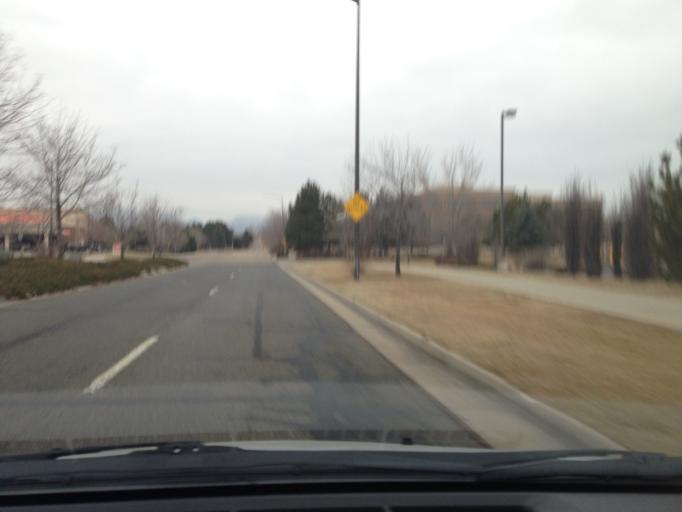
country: US
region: Colorado
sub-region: Boulder County
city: Superior
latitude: 39.9621
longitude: -105.1673
